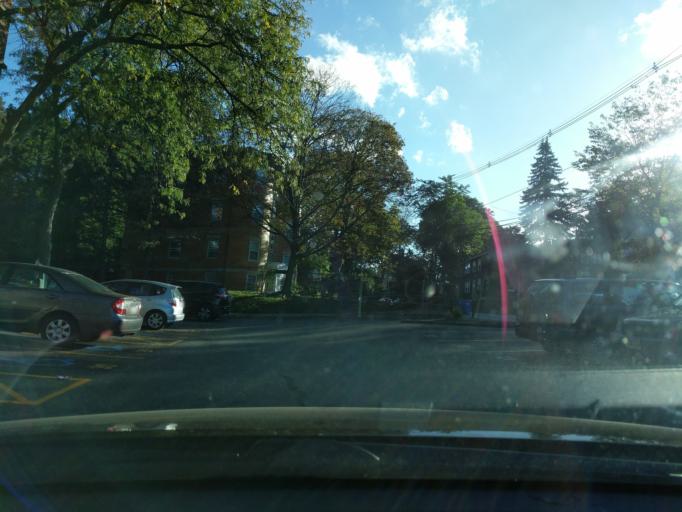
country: US
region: Massachusetts
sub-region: Norfolk County
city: Brookline
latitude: 42.3308
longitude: -71.1176
